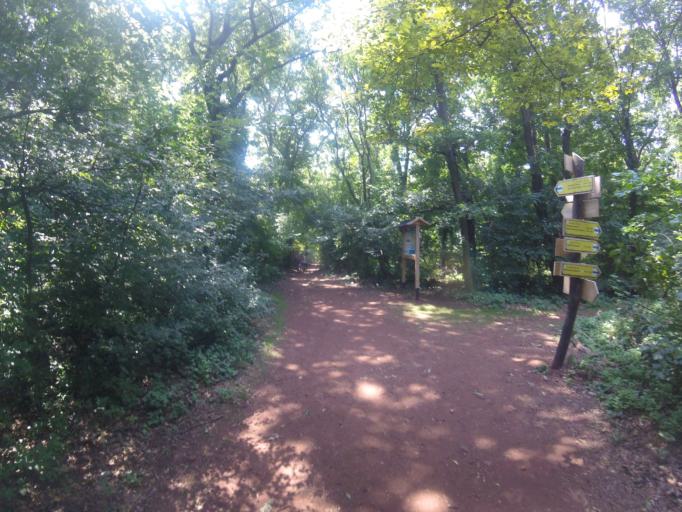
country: HU
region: Veszprem
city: Badacsonytomaj
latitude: 46.8028
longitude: 17.4963
